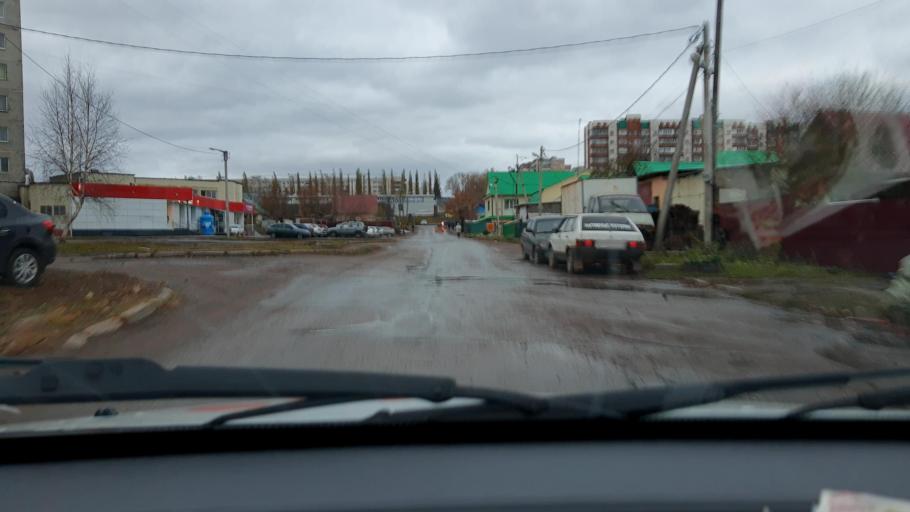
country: RU
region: Bashkortostan
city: Ufa
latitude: 54.8212
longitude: 56.1242
